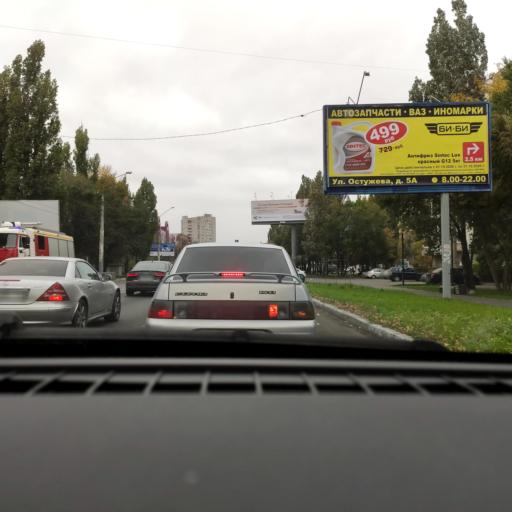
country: RU
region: Voronezj
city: Voronezh
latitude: 51.6704
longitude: 39.2578
